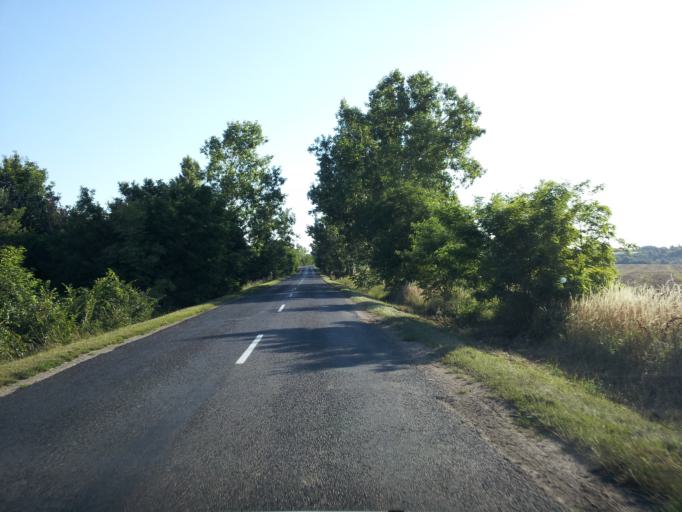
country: HU
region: Fejer
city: Lepseny
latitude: 47.0433
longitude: 18.2357
